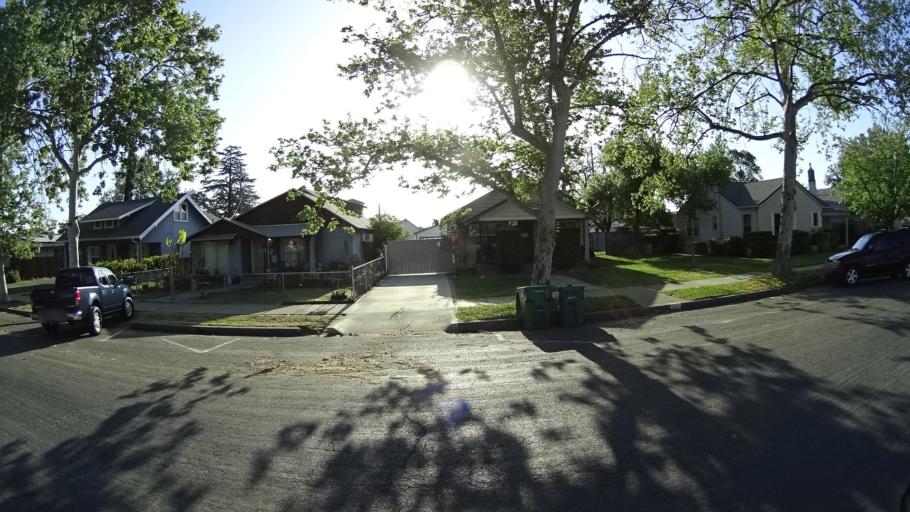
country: US
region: California
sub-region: Glenn County
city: Orland
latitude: 39.7480
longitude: -122.1902
